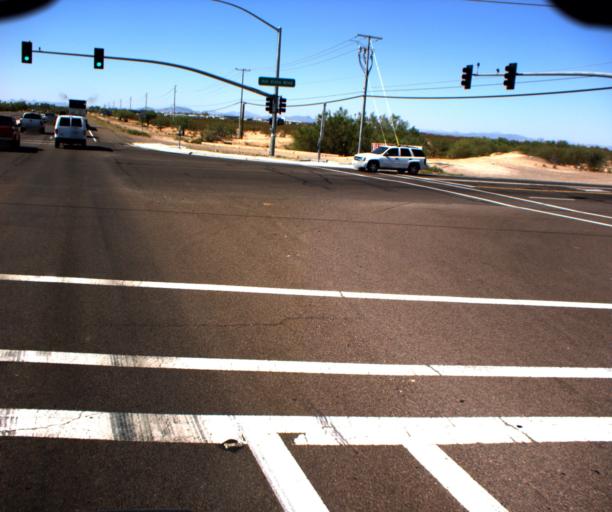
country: US
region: Arizona
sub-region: Pinal County
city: Casa Grande
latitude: 32.9678
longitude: -111.7569
